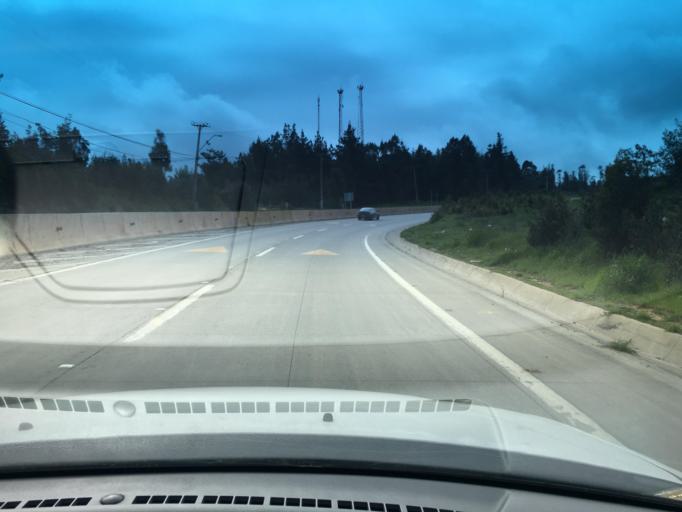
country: CL
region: Valparaiso
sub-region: Provincia de Valparaiso
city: Vina del Mar
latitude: -33.1053
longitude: -71.5729
